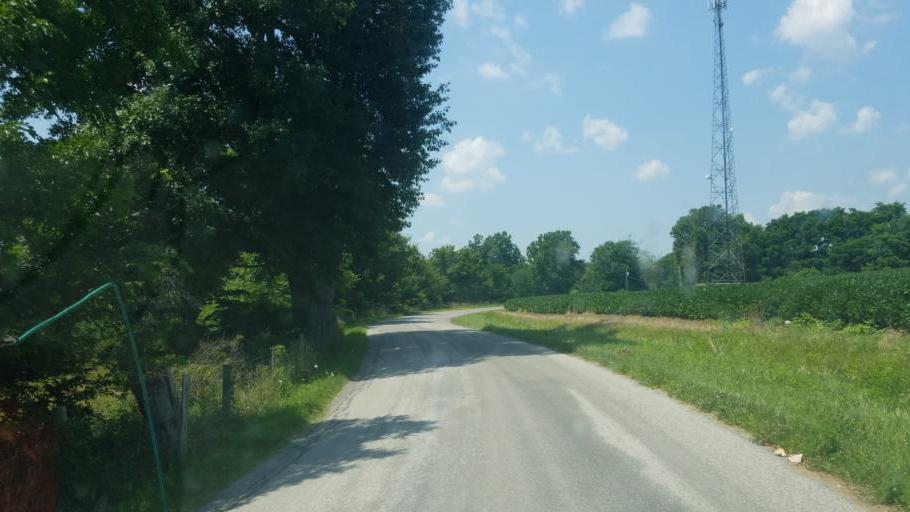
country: US
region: Ohio
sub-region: Richland County
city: Shelby
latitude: 40.8449
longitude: -82.6540
